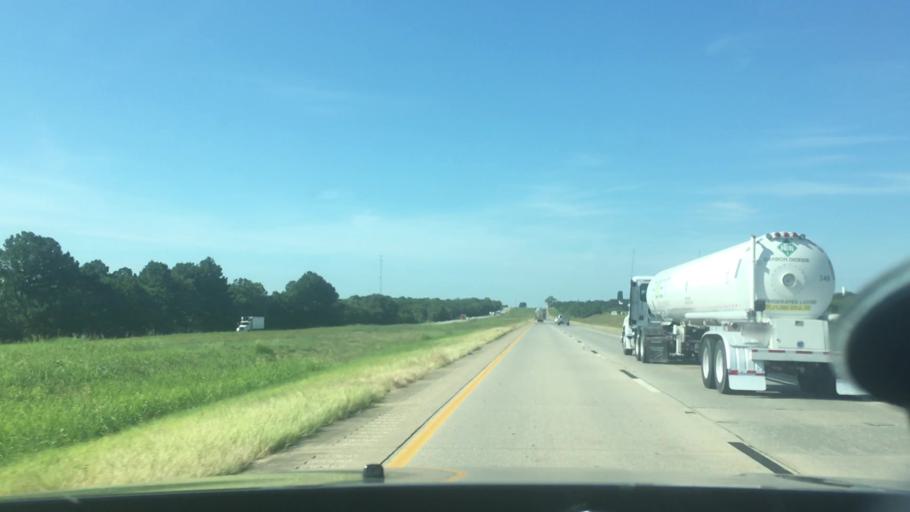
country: US
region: Oklahoma
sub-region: Atoka County
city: Atoka
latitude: 34.1930
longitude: -96.2423
